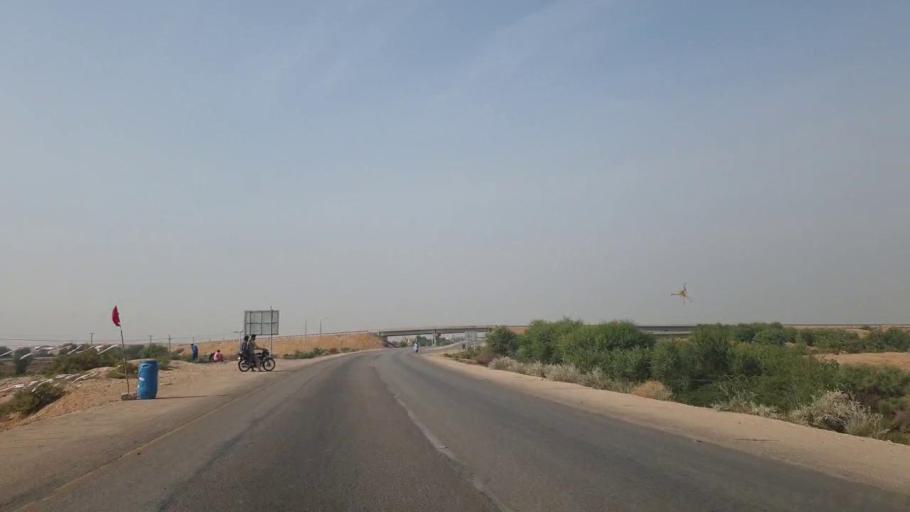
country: PK
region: Sindh
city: Sann
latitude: 26.1533
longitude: 68.0255
